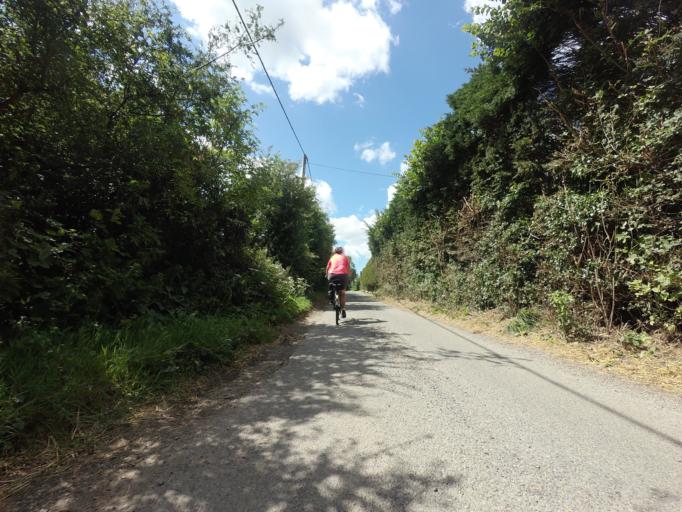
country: GB
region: England
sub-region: East Sussex
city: Hailsham
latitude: 50.8677
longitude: 0.1635
